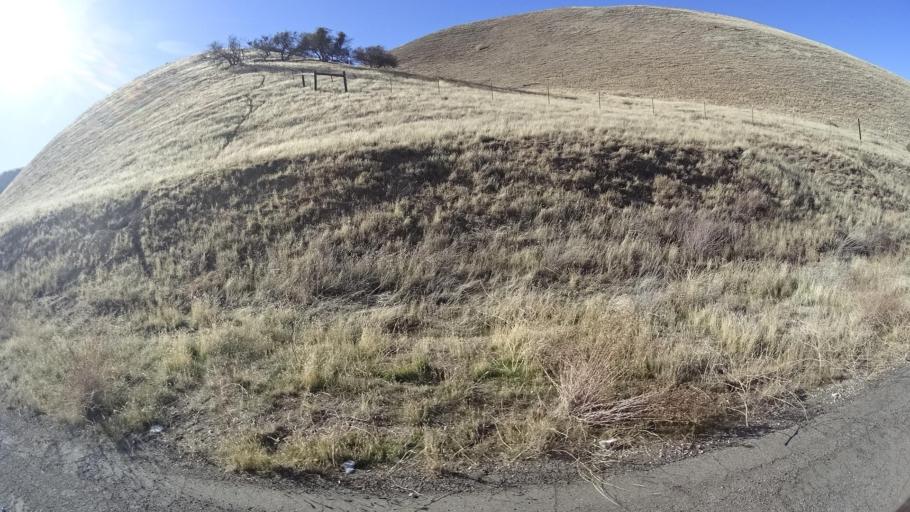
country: US
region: California
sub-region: Kern County
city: Maricopa
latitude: 34.9519
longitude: -119.4067
